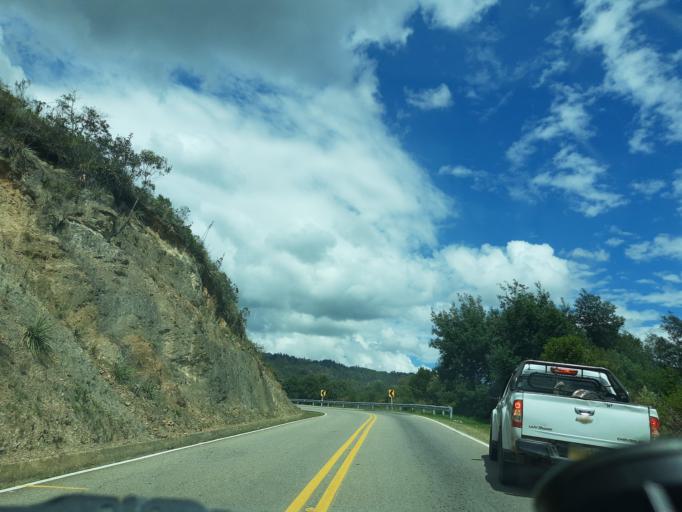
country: CO
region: Boyaca
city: Raquira
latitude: 5.5843
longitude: -73.6852
